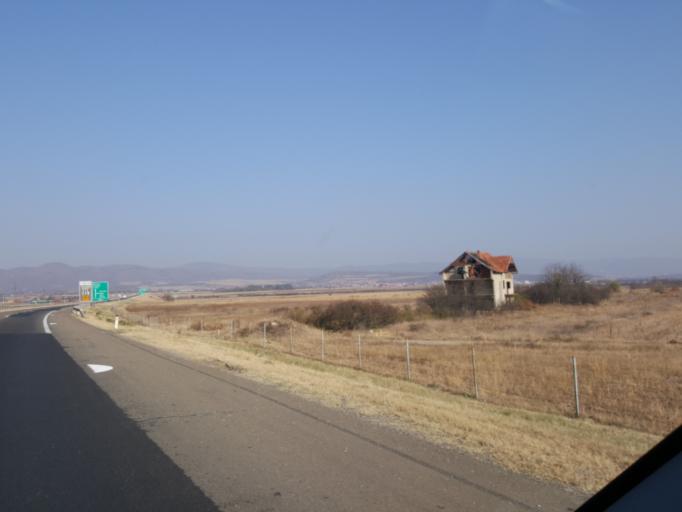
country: RS
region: Central Serbia
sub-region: Nisavski Okrug
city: Nis
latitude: 43.3422
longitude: 21.8166
